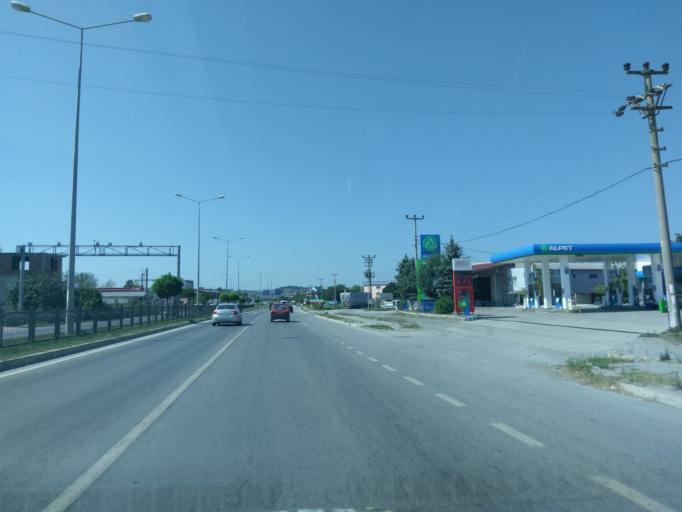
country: TR
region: Samsun
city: Bafra
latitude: 41.5689
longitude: 35.8777
